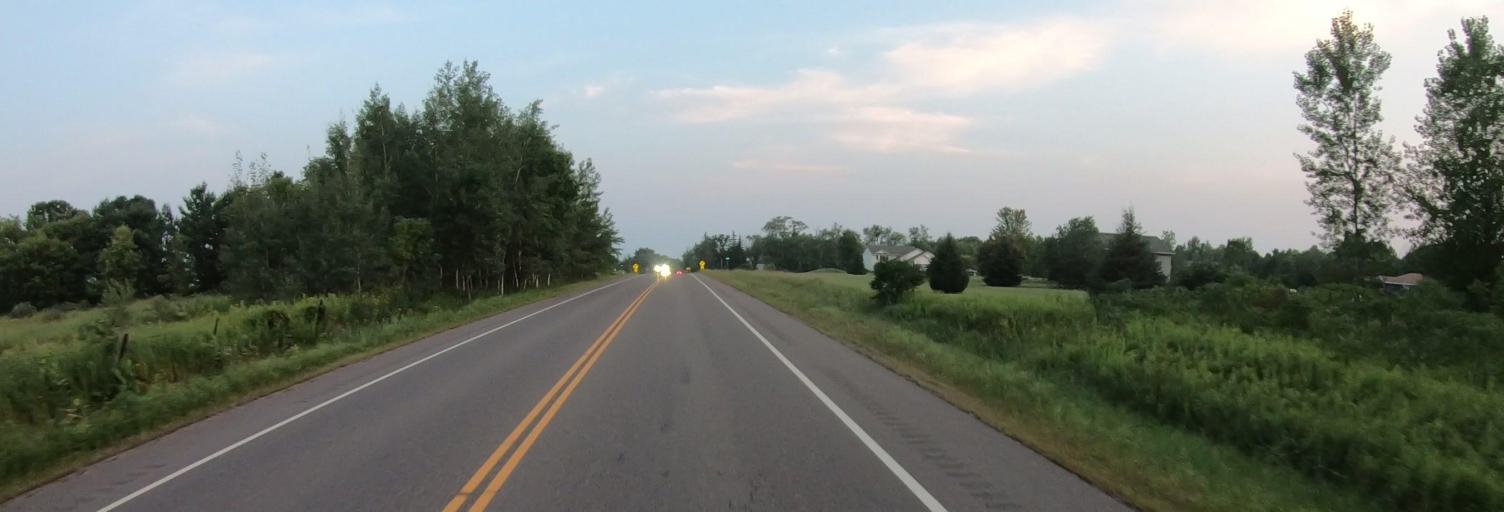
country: US
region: Minnesota
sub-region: Pine County
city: Rock Creek
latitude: 45.7696
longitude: -92.9602
